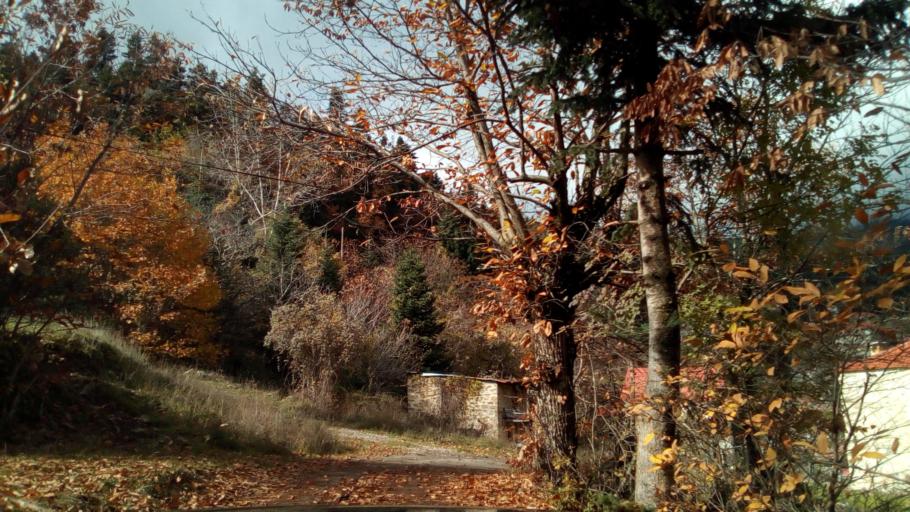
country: GR
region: Central Greece
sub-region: Nomos Fokidos
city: Lidoriki
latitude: 38.5807
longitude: 21.9780
